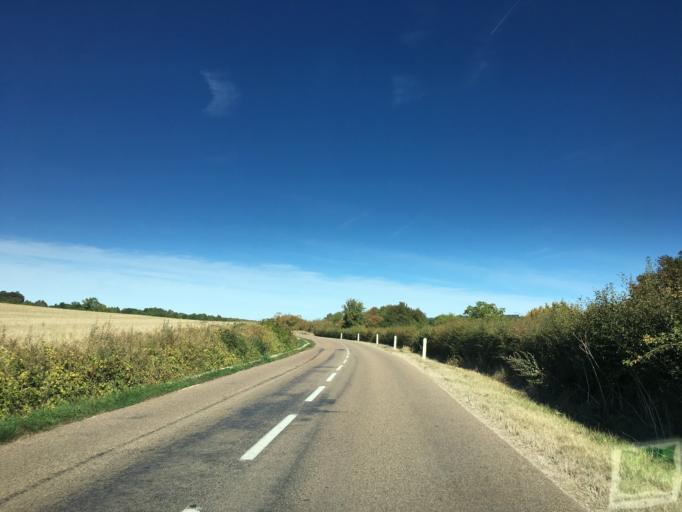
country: FR
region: Bourgogne
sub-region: Departement de l'Yonne
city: Vermenton
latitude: 47.6106
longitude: 3.6780
